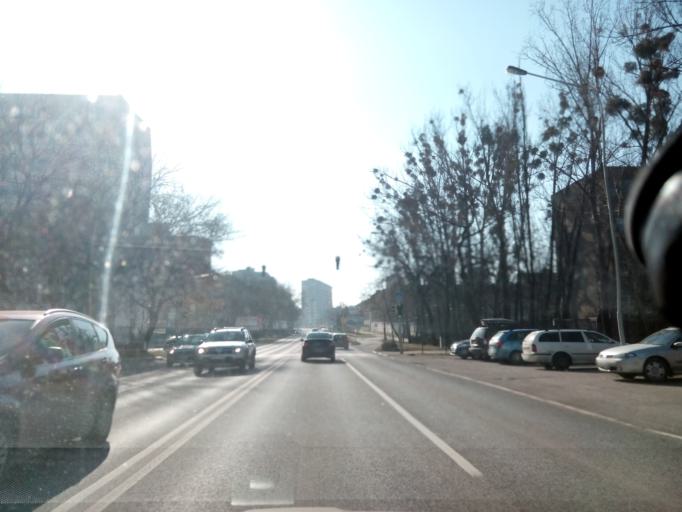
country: SK
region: Kosicky
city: Kosice
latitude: 48.7313
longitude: 21.2390
